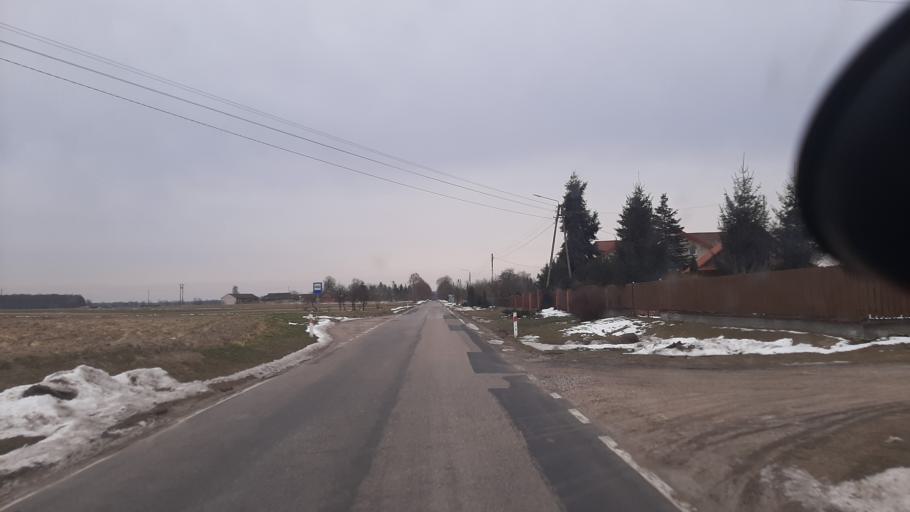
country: PL
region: Lublin Voivodeship
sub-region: Powiat lubartowski
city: Kamionka
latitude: 51.4642
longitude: 22.4201
